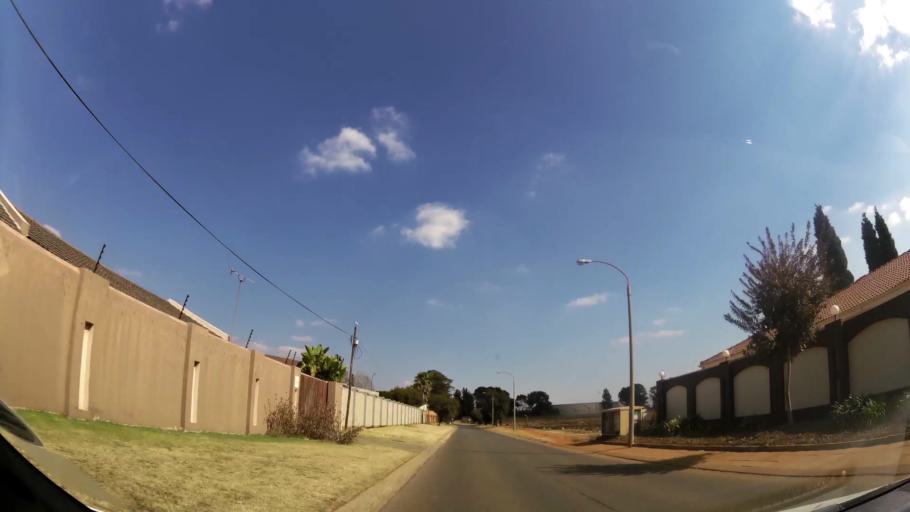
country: ZA
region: Gauteng
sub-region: Ekurhuleni Metropolitan Municipality
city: Boksburg
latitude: -26.1873
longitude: 28.2342
